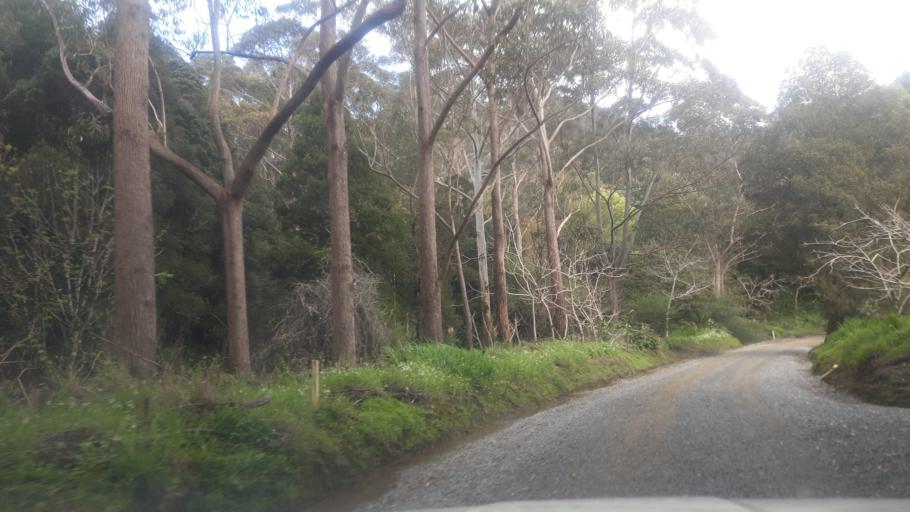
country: NZ
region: Northland
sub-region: Far North District
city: Taipa
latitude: -35.1122
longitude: 173.4265
